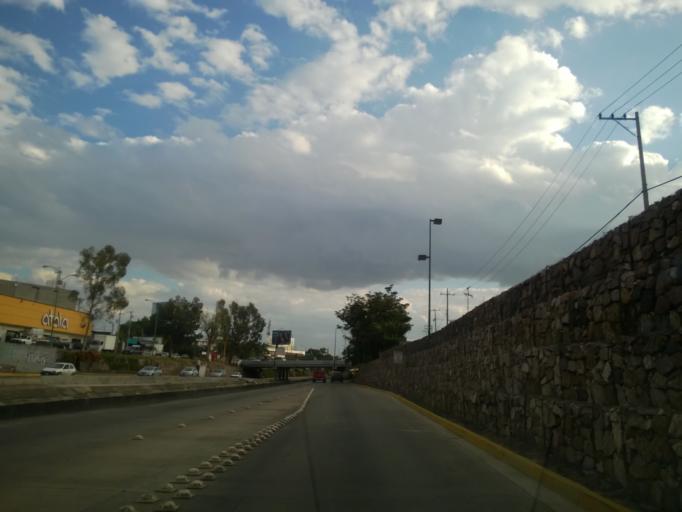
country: MX
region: Guanajuato
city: Leon
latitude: 21.1361
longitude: -101.6790
